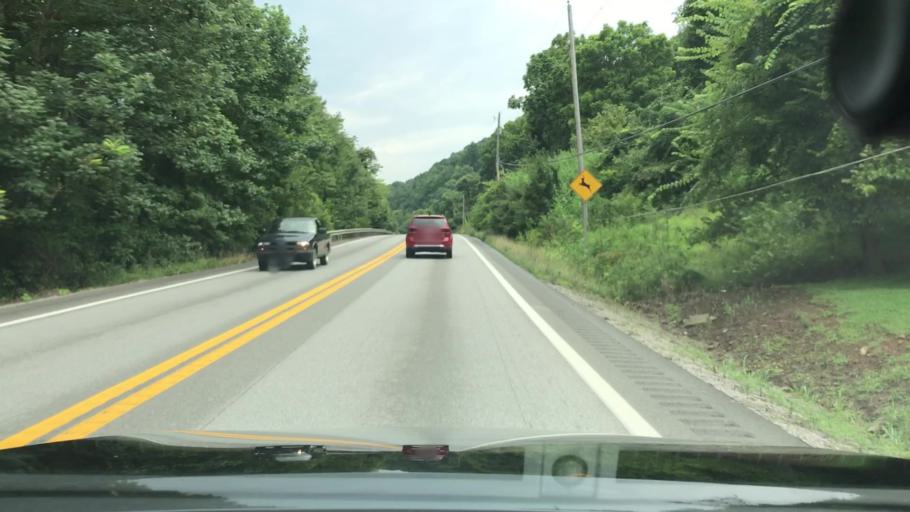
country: US
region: West Virginia
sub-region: Putnam County
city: Buffalo
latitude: 38.6056
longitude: -82.0012
